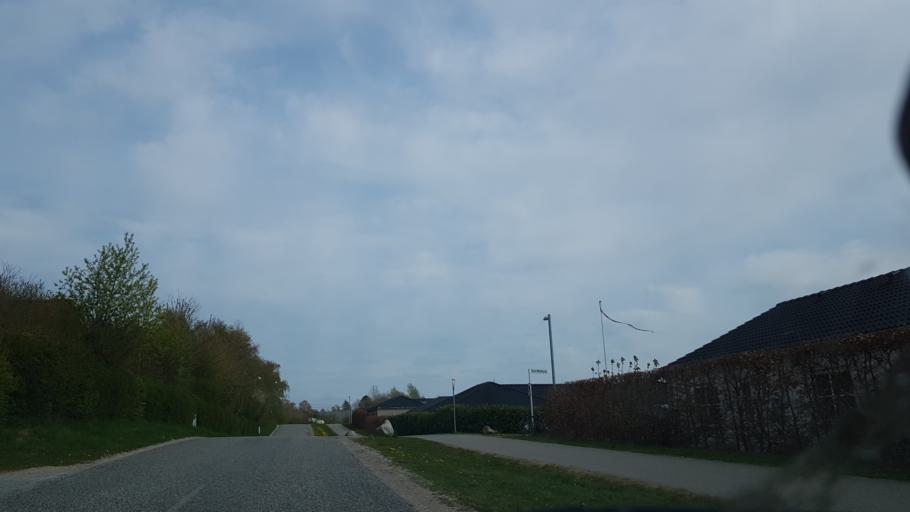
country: DK
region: Capital Region
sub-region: Allerod Kommune
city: Lillerod
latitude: 55.8841
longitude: 12.3424
